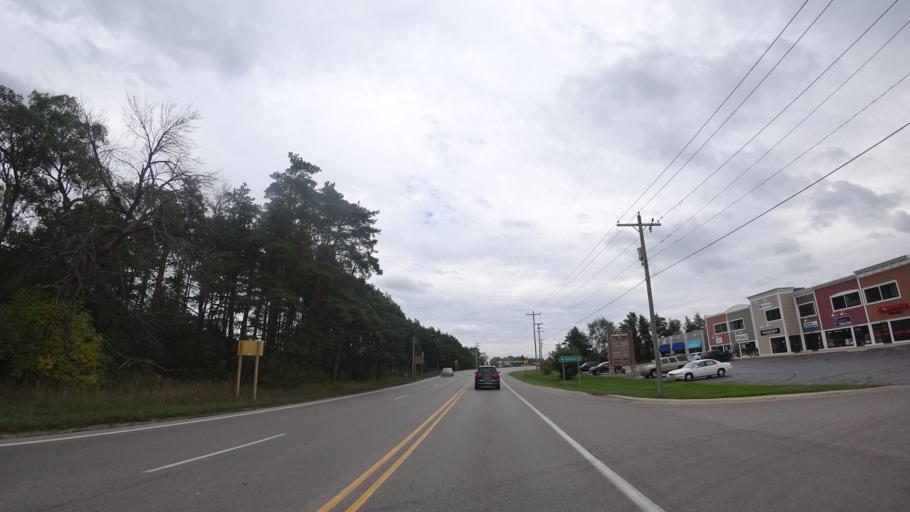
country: US
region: Michigan
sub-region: Emmet County
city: Petoskey
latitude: 45.4279
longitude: -84.9084
